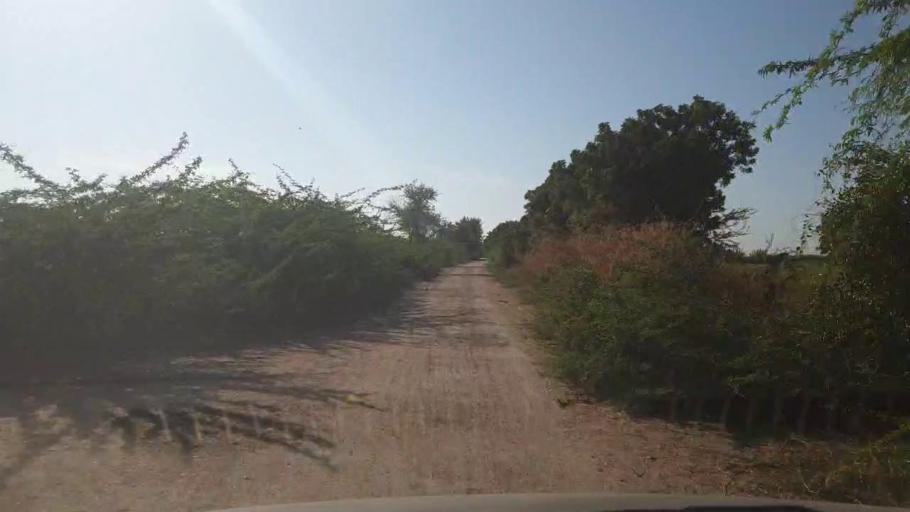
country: PK
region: Sindh
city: Dhoro Naro
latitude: 25.4126
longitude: 69.5687
